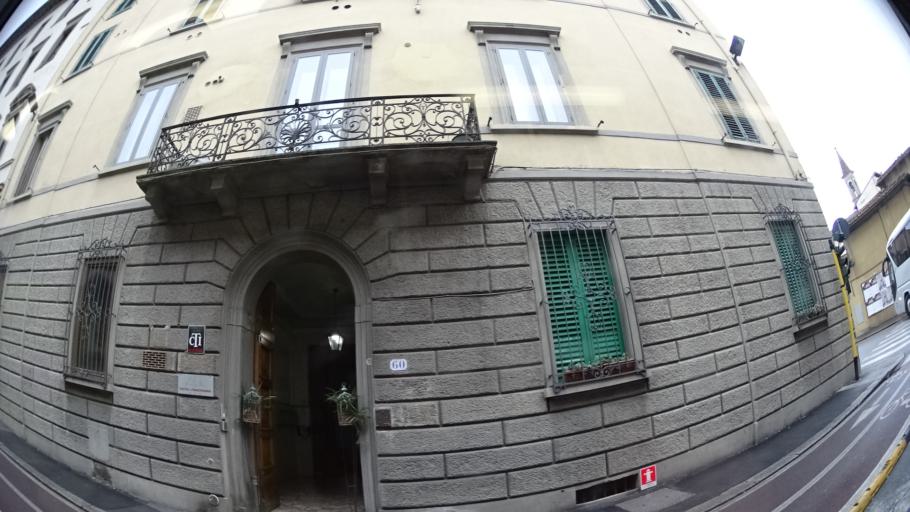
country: IT
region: Tuscany
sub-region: Province of Florence
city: Florence
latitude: 43.7808
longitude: 11.2615
